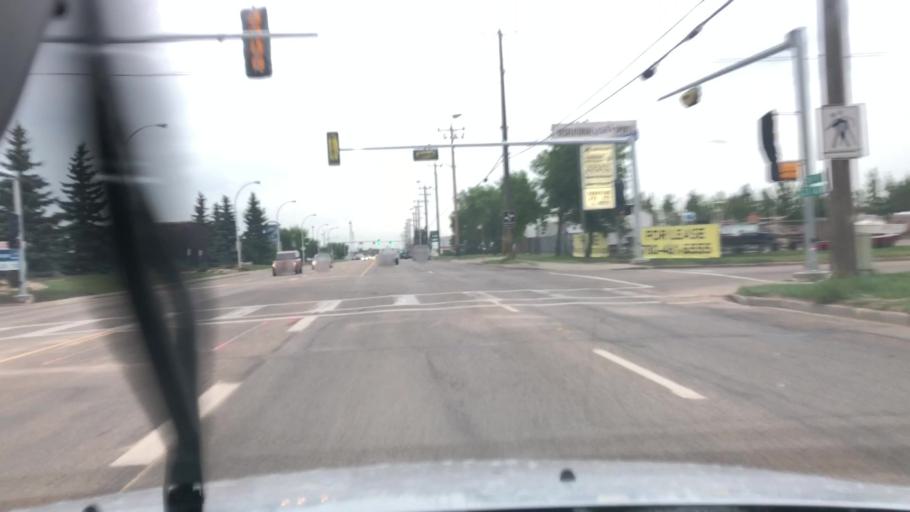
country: CA
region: Alberta
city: St. Albert
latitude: 53.5766
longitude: -113.5779
